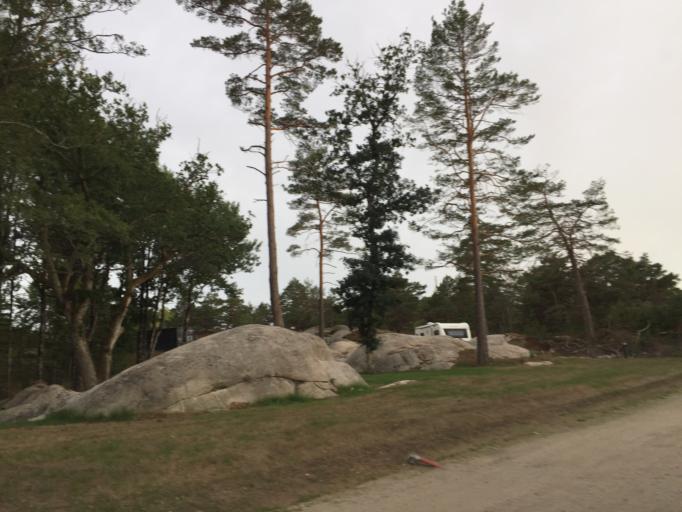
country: NO
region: Ostfold
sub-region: Hvaler
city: Skjaerhalden
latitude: 59.0568
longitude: 11.0095
